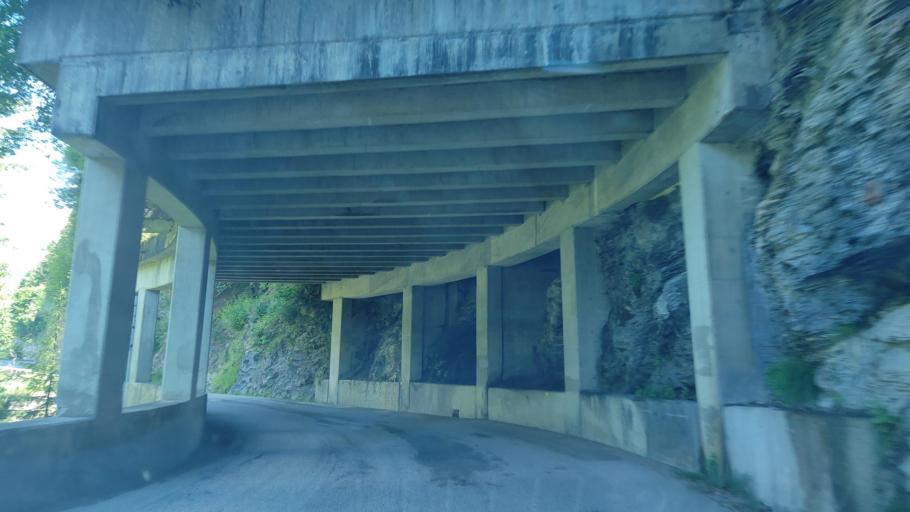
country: FR
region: Rhone-Alpes
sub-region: Departement de la Haute-Savoie
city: Praz-sur-Arly
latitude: 45.8294
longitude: 6.5102
